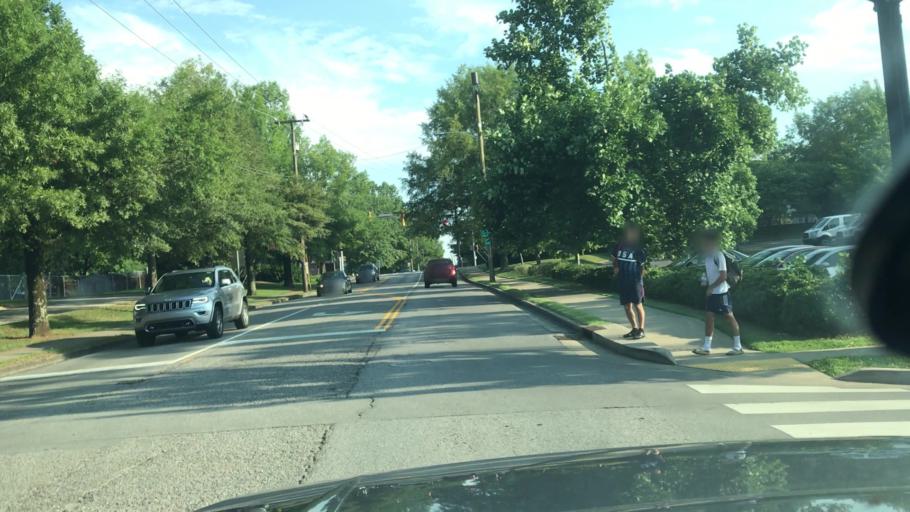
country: US
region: Tennessee
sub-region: Davidson County
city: Nashville
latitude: 36.1397
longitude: -86.8107
